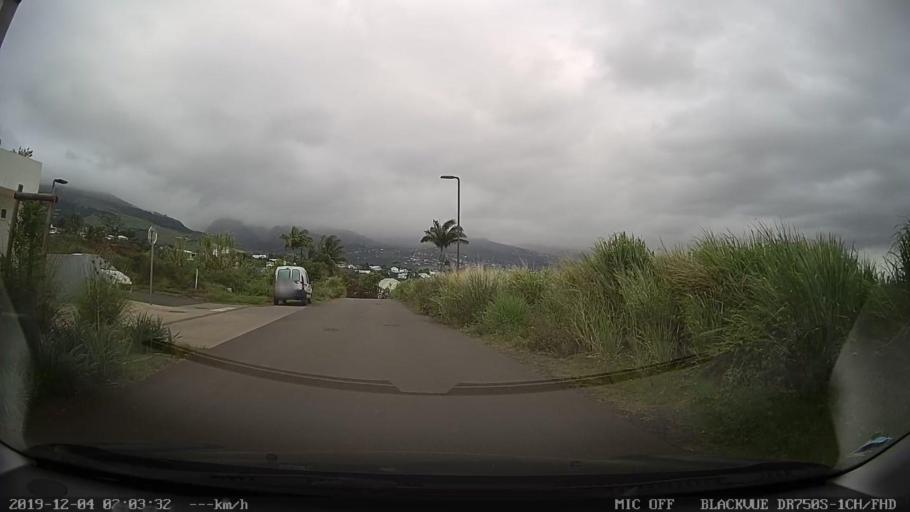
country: RE
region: Reunion
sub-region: Reunion
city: Sainte-Marie
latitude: -20.9213
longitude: 55.5258
